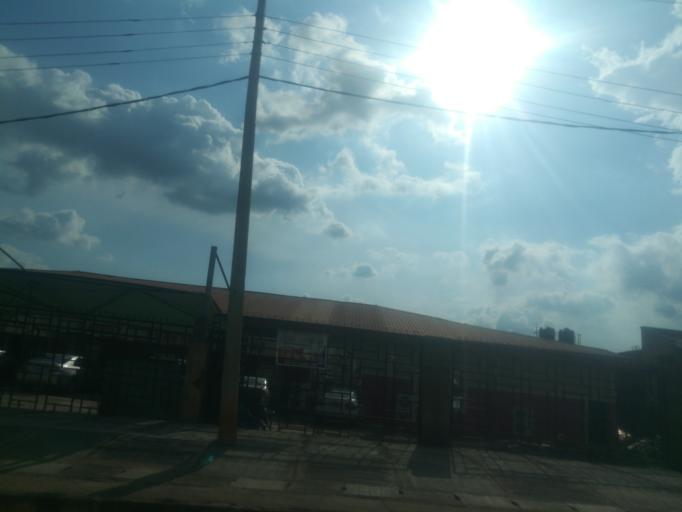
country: NG
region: Oyo
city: Ibadan
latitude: 7.4219
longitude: 3.8440
